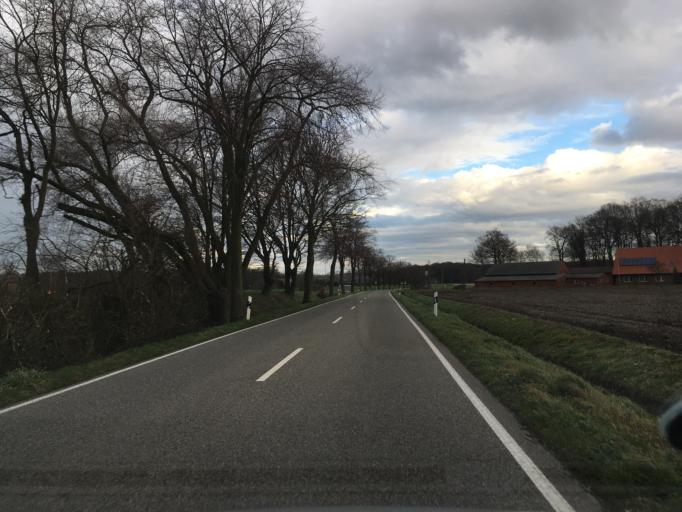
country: DE
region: North Rhine-Westphalia
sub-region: Regierungsbezirk Munster
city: Schoppingen
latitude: 52.0771
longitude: 7.2080
